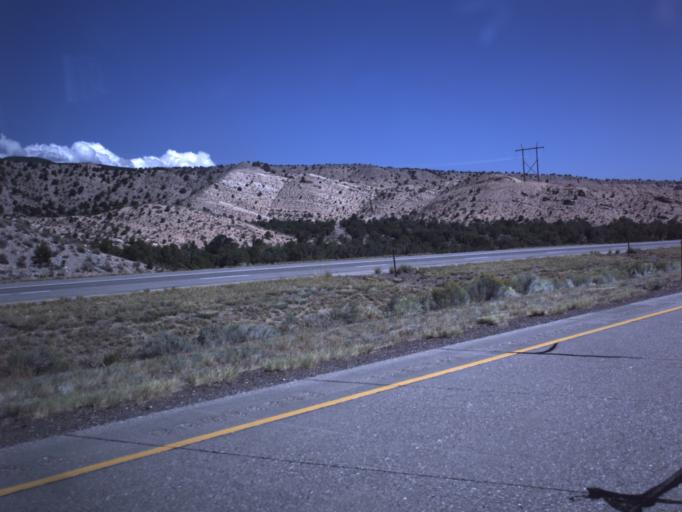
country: US
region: Utah
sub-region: Sevier County
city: Monroe
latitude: 38.5972
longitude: -112.2619
